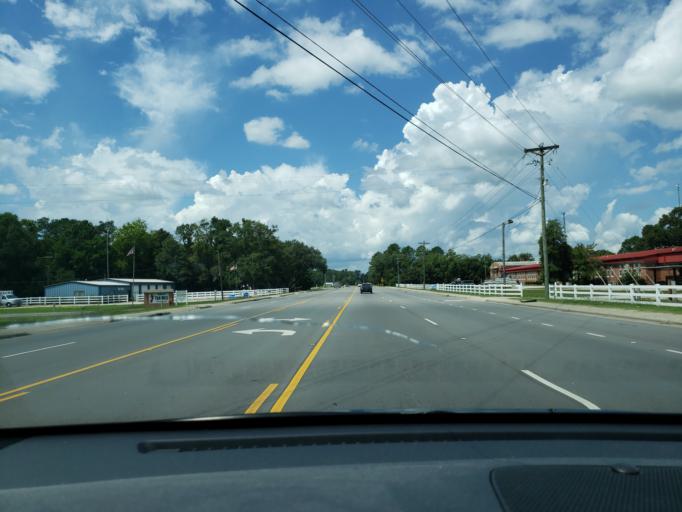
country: US
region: North Carolina
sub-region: Robeson County
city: Saint Pauls
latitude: 34.7352
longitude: -78.7941
